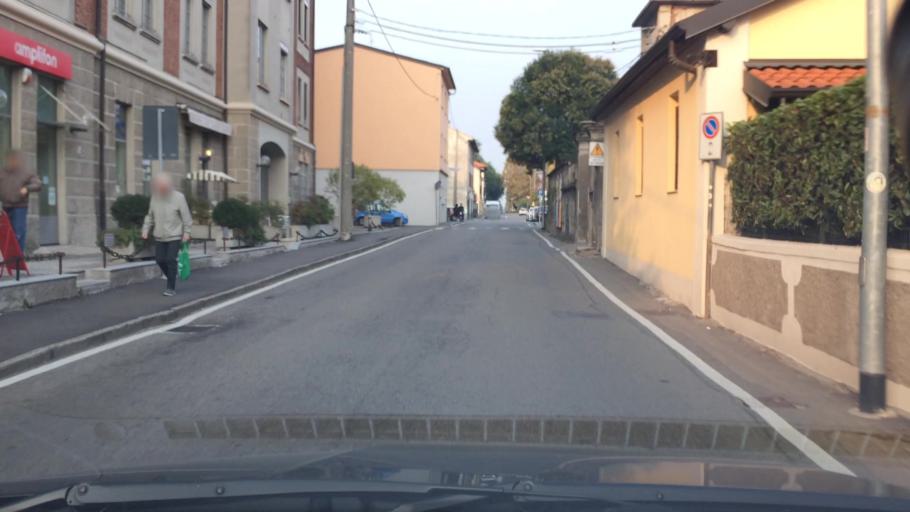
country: IT
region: Lombardy
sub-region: Provincia di Como
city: Lomazzo
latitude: 45.6986
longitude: 9.0347
